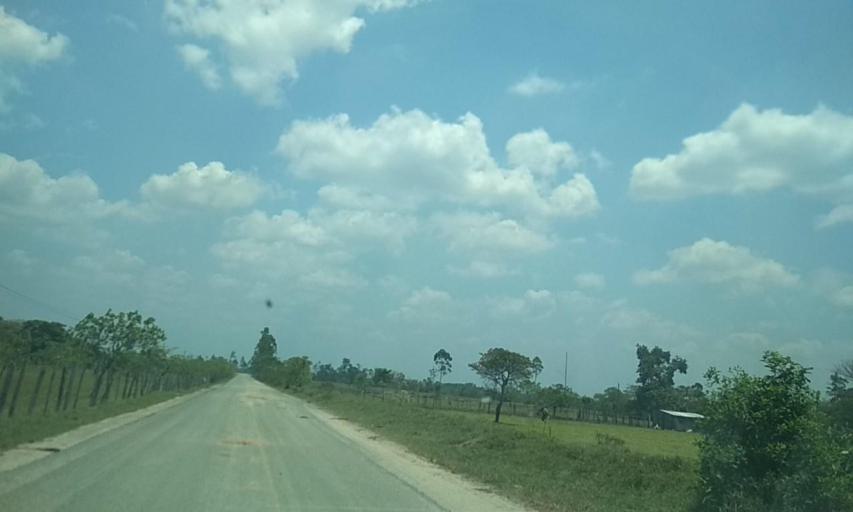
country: MX
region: Tabasco
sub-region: Huimanguillo
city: Francisco Rueda
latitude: 17.8122
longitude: -93.8692
